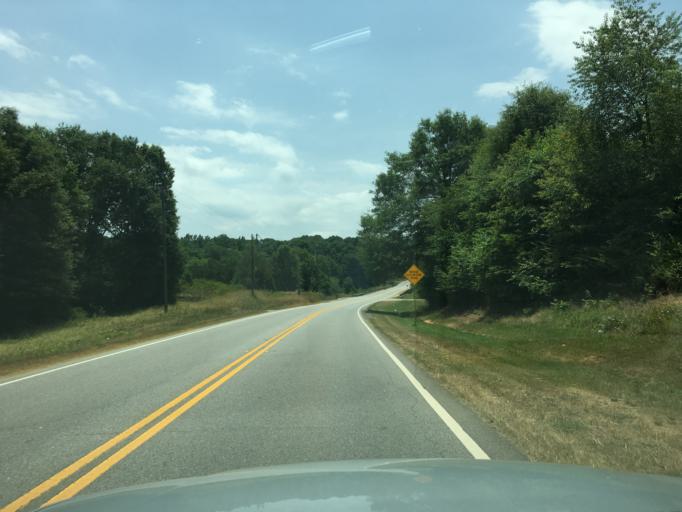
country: US
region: Georgia
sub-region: Hart County
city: Royston
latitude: 34.2492
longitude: -83.1725
